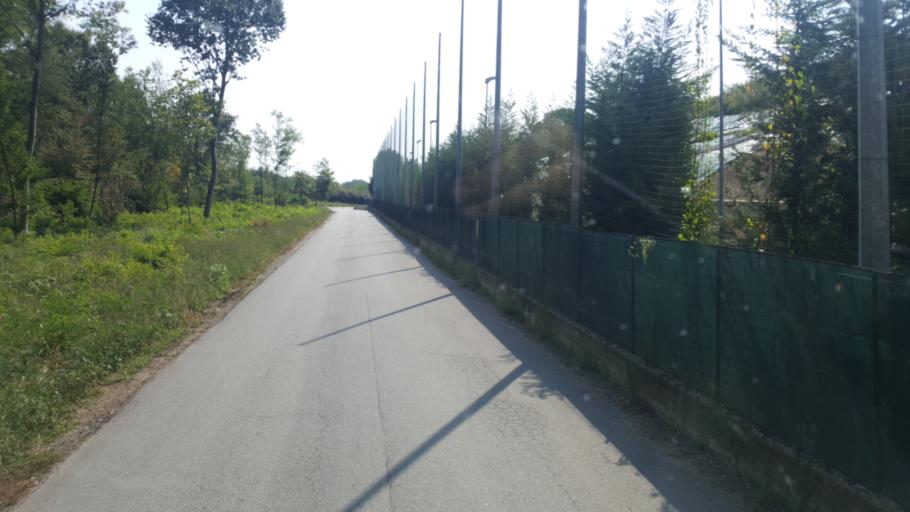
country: IT
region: Lombardy
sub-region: Provincia di Como
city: Carbonate
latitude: 45.6674
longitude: 8.9240
